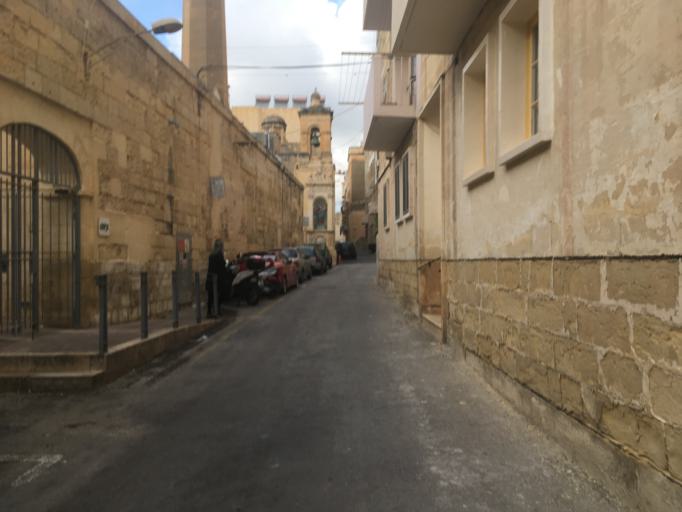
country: MT
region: L-Isla
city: Senglea
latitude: 35.8883
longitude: 14.5209
